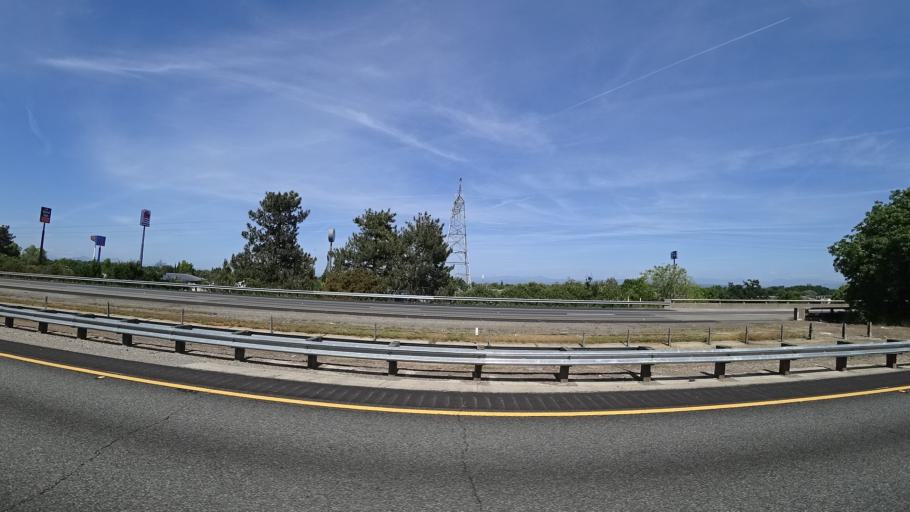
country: US
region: California
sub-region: Shasta County
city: Anderson
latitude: 40.4522
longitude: -122.2921
